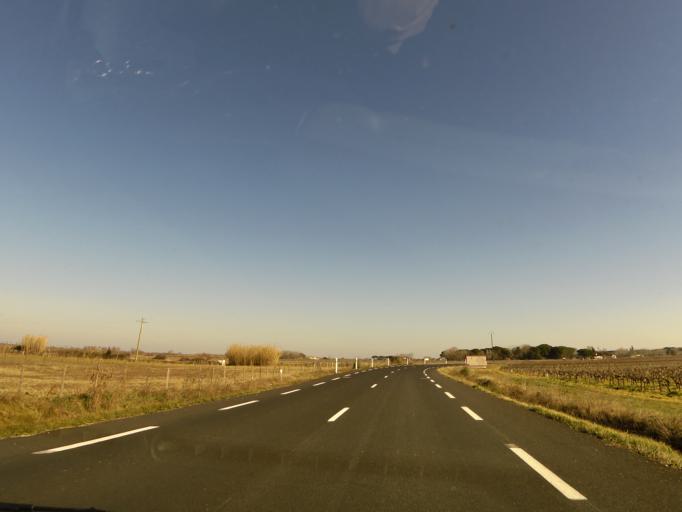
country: FR
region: Languedoc-Roussillon
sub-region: Departement du Gard
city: Aigues-Mortes
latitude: 43.5874
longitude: 4.2228
